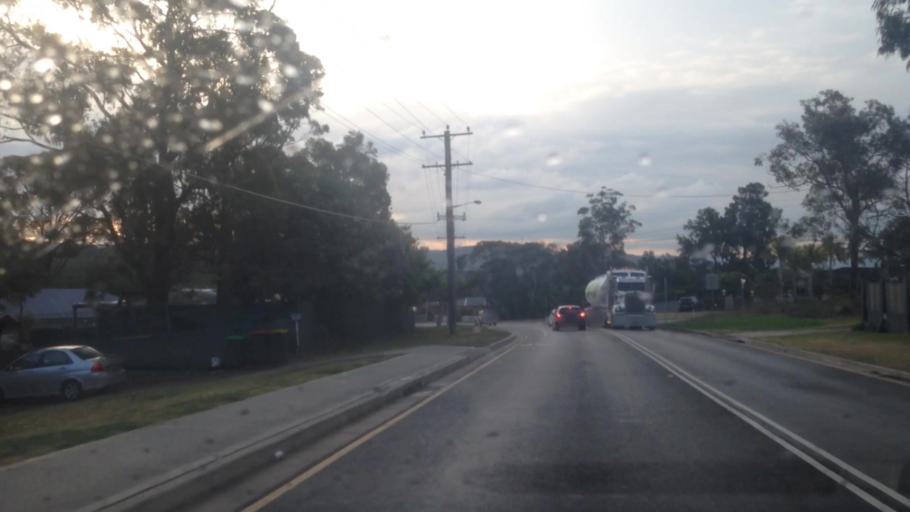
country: AU
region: New South Wales
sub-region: Wyong Shire
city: Charmhaven
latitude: -33.1851
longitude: 151.4911
